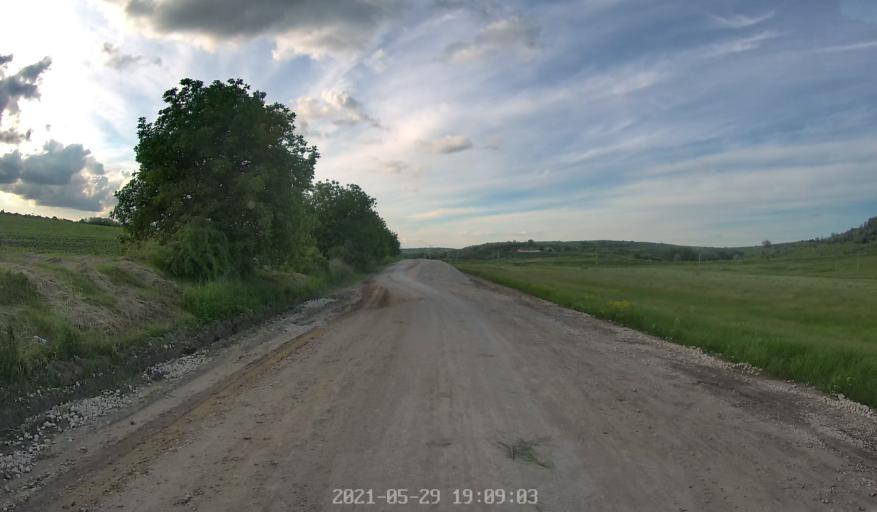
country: MD
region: Chisinau
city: Singera
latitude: 46.8306
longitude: 28.9563
